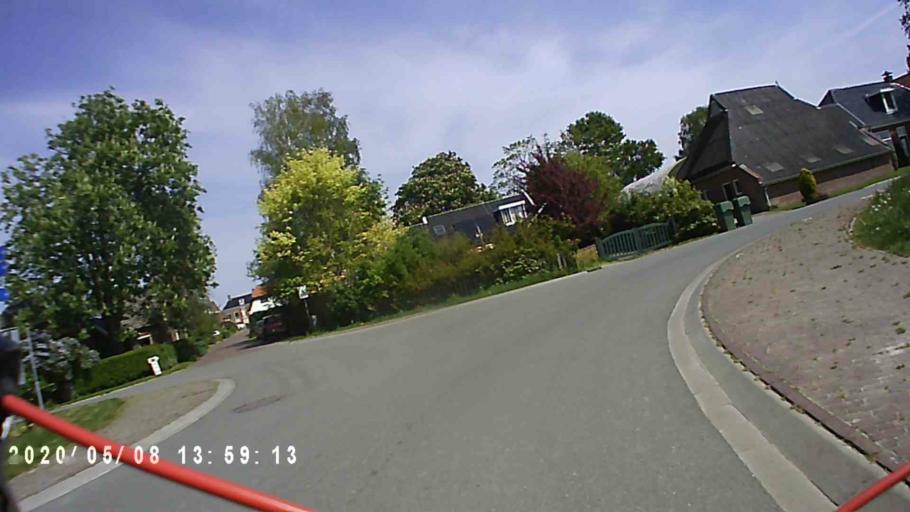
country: NL
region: Groningen
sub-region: Gemeente Appingedam
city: Appingedam
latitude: 53.3374
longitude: 6.8124
